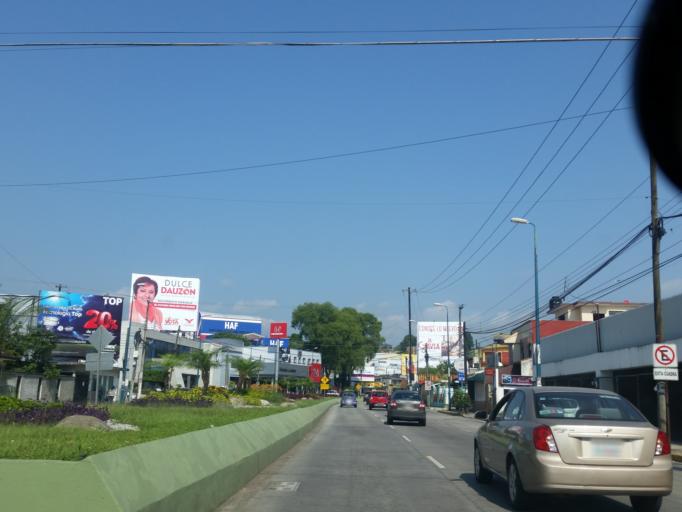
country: MX
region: Veracruz
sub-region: Xalapa
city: Xalapa de Enriquez
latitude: 19.5216
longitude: -96.9081
